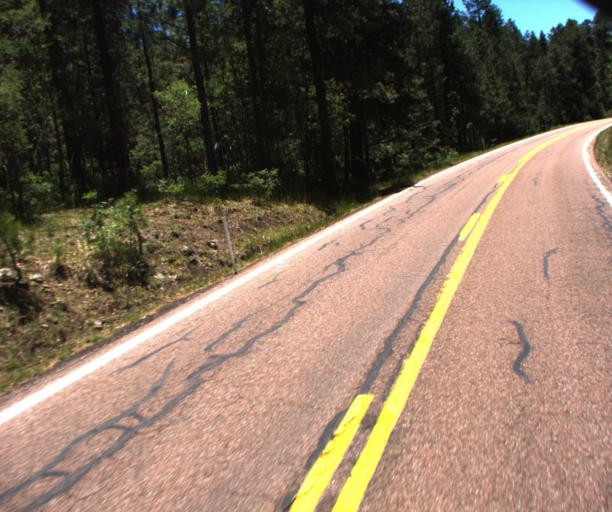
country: US
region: Arizona
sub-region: Gila County
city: Pine
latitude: 34.4660
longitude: -111.3831
